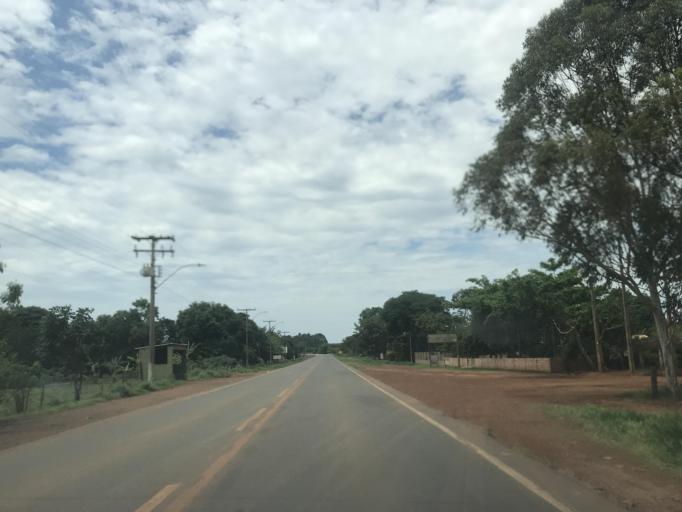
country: BR
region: Goias
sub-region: Luziania
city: Luziania
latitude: -16.3211
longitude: -48.0181
